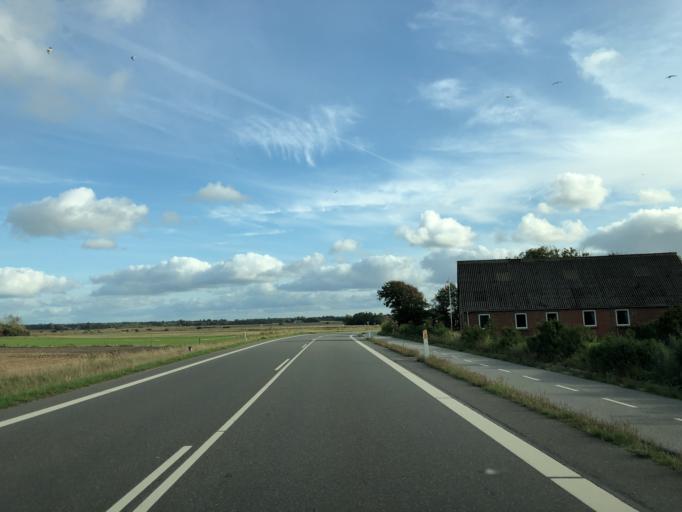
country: DK
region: Central Jutland
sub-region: Holstebro Kommune
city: Ulfborg
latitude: 56.2940
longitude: 8.3387
